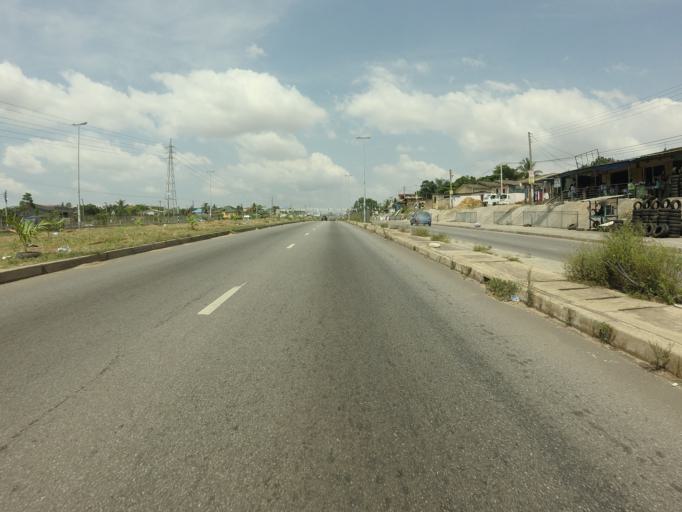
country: GH
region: Greater Accra
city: Gbawe
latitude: 5.5932
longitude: -0.2886
